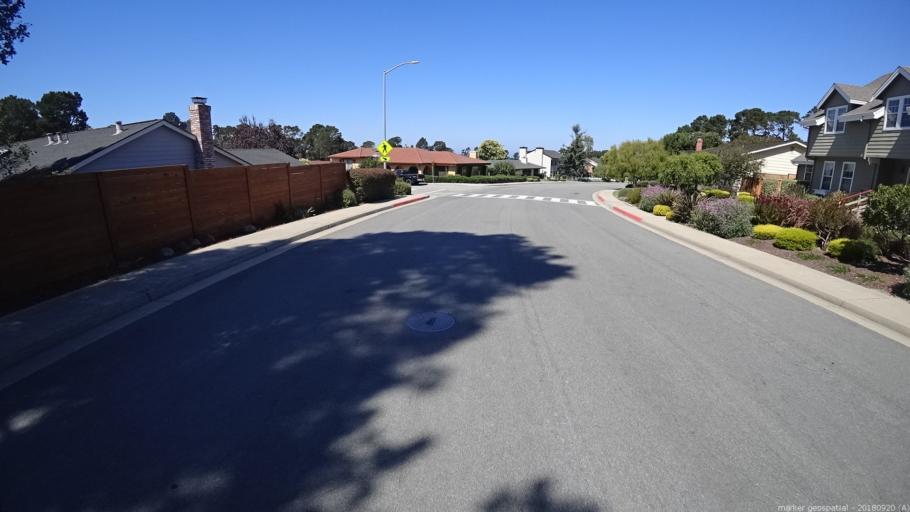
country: US
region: California
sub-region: Monterey County
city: Del Rey Oaks
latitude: 36.5779
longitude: -121.8624
